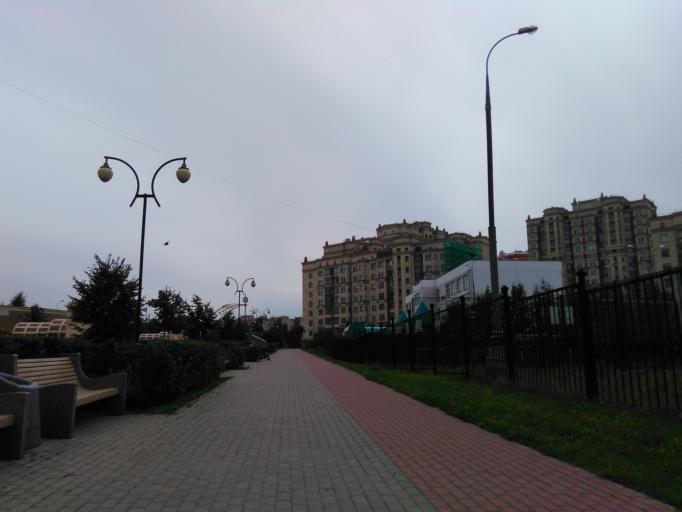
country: RU
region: Moscow
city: Ramenki
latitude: 55.7027
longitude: 37.5137
